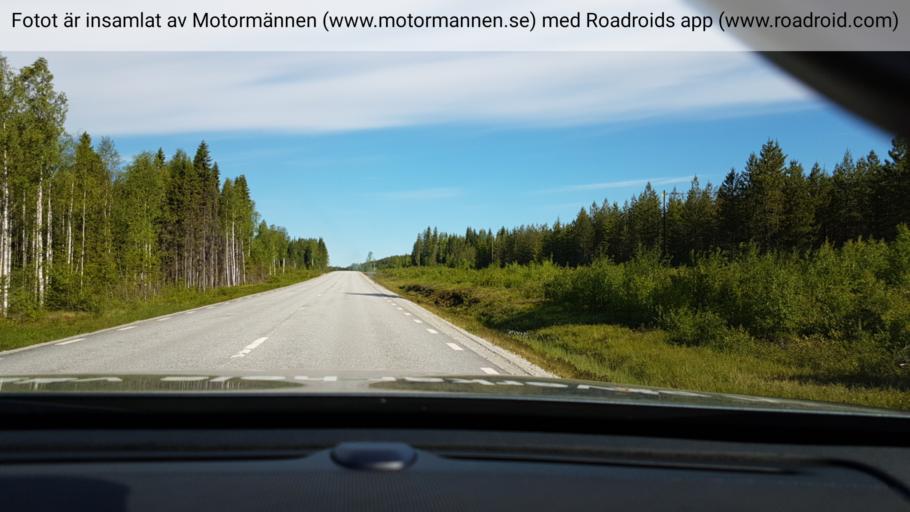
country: SE
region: Vaesterbotten
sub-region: Vindelns Kommun
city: Vindeln
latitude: 64.1911
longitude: 19.4620
